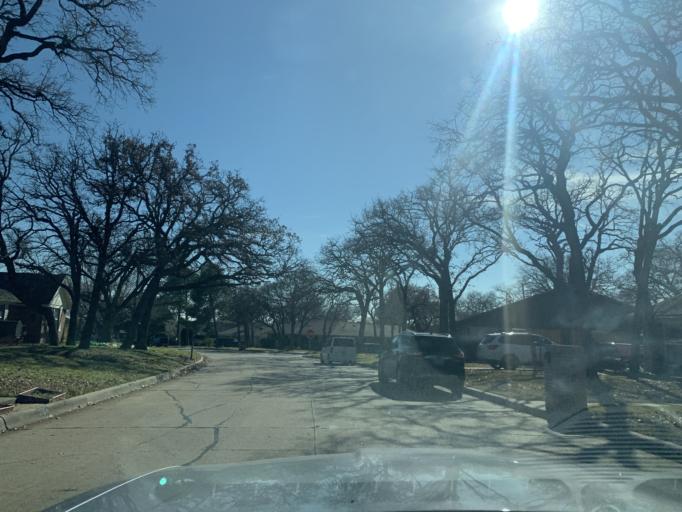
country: US
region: Texas
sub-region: Tarrant County
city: Bedford
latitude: 32.8421
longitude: -97.1563
